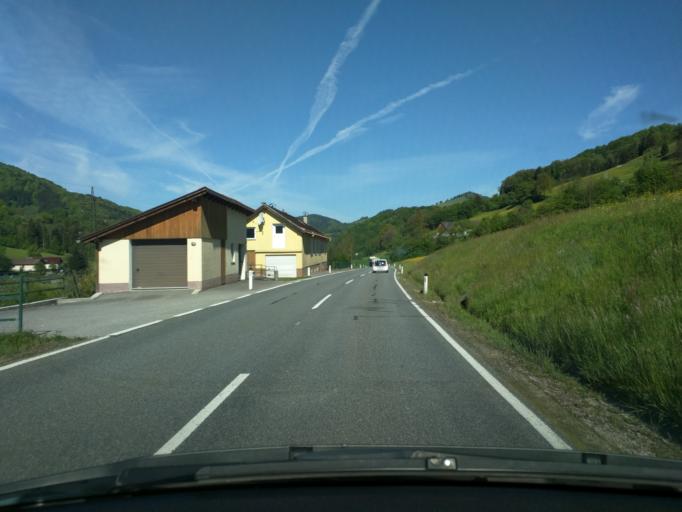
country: AT
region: Lower Austria
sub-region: Politischer Bezirk Scheibbs
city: Randegg
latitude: 48.0060
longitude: 14.9940
